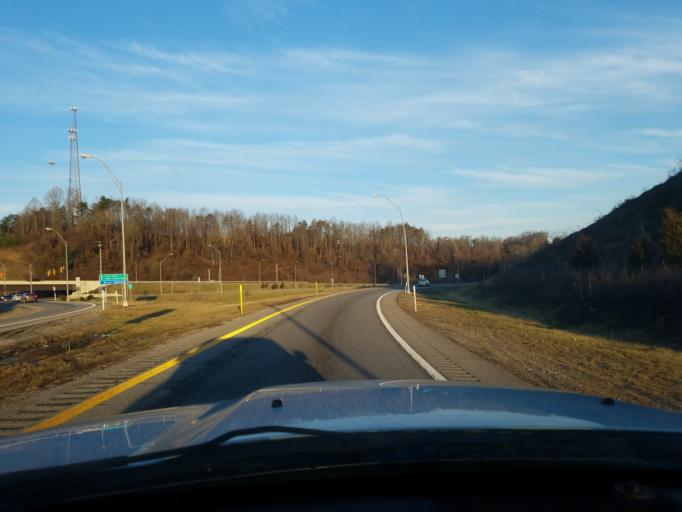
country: US
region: West Virginia
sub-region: Putnam County
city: Teays Valley
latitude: 38.4551
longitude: -81.9023
